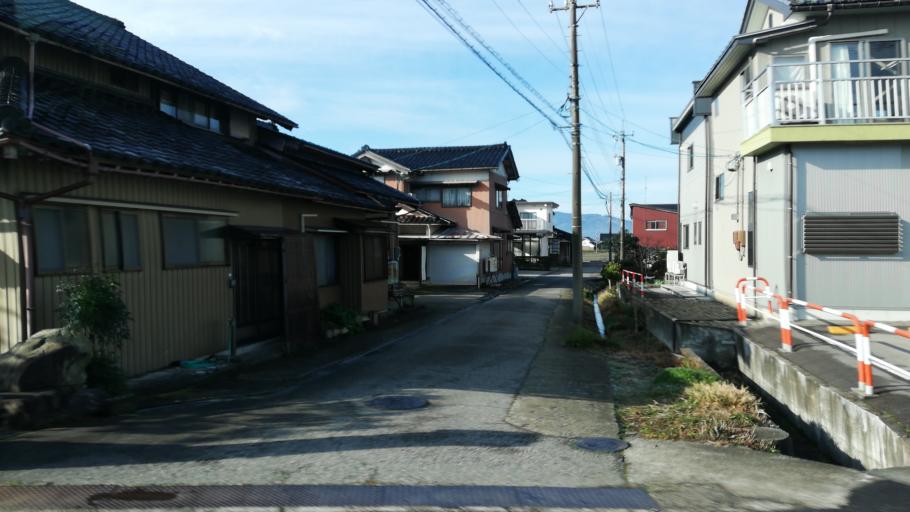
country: JP
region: Toyama
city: Nanto-shi
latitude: 36.5829
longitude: 136.9230
